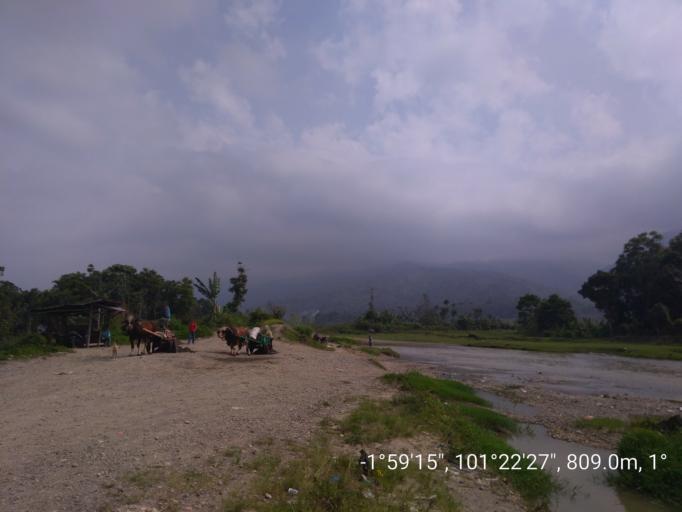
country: ID
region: Jambi
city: Semurup
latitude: -1.9878
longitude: 101.3741
